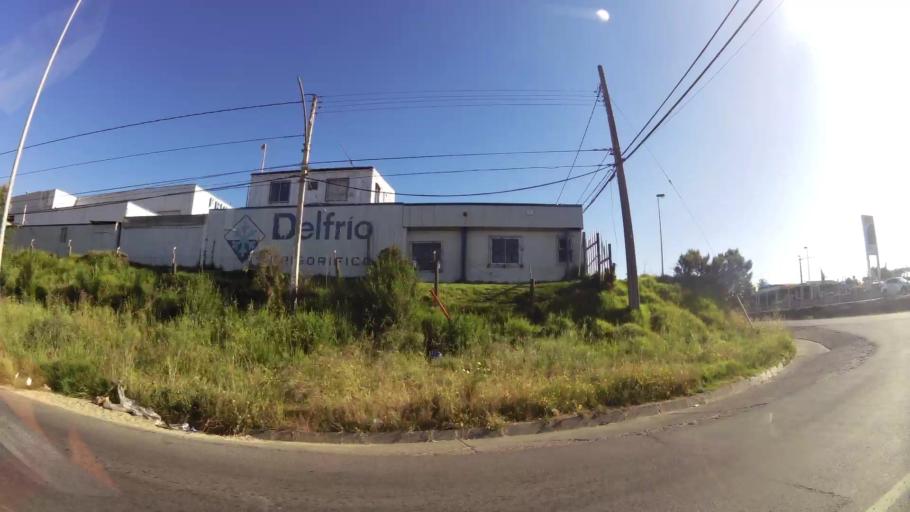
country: CL
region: Valparaiso
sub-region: Provincia de Valparaiso
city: Vina del Mar
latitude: -33.1172
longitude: -71.5602
